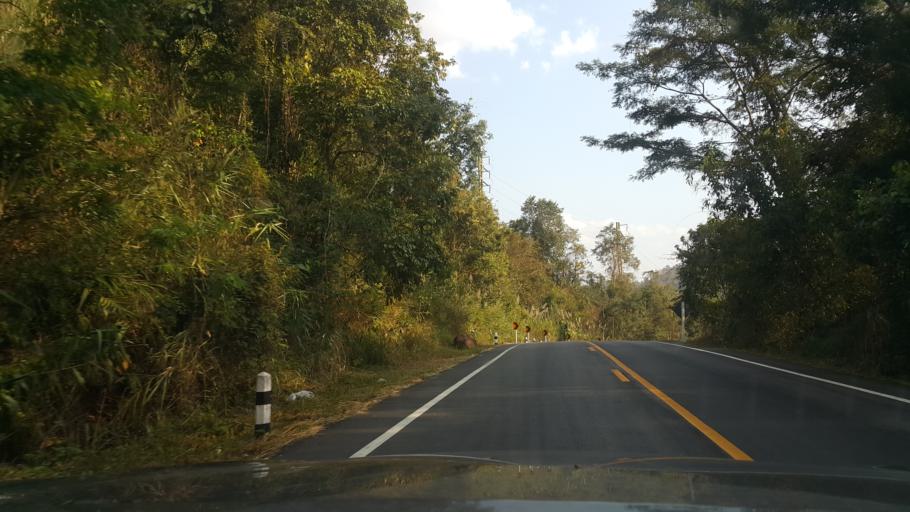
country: TH
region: Loei
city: Dan Sai
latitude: 17.2286
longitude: 101.0749
